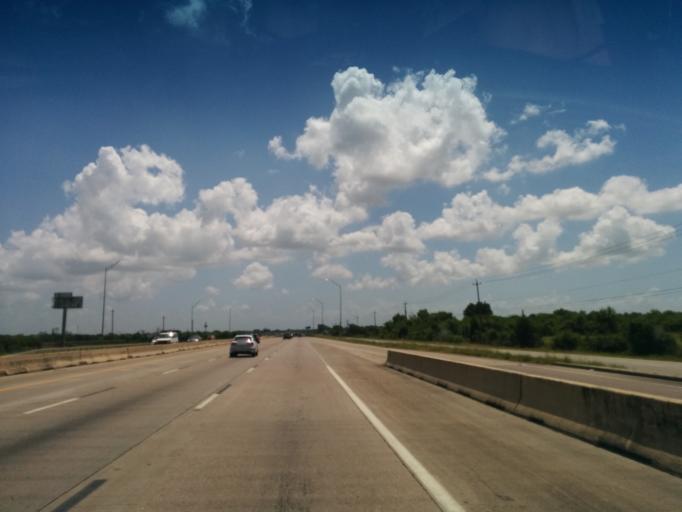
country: US
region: Texas
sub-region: Harris County
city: Baytown
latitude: 29.8085
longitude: -94.9605
